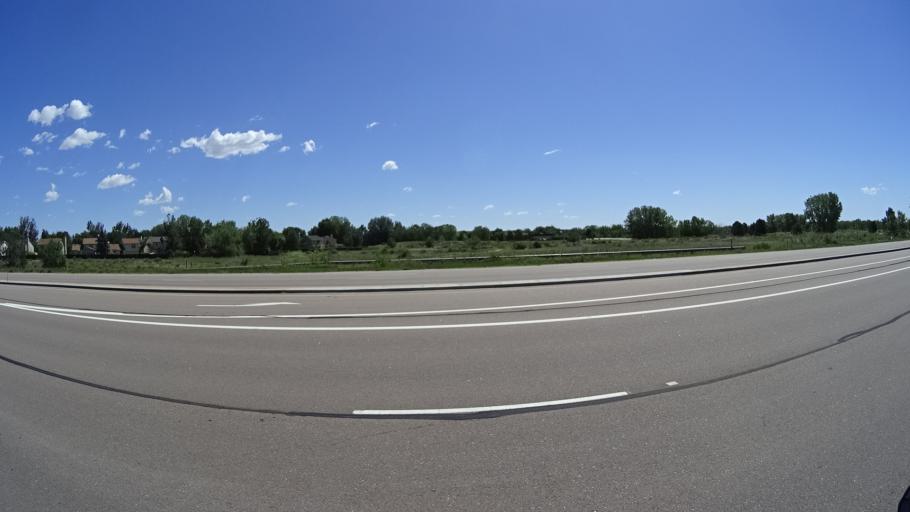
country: US
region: Colorado
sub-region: El Paso County
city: Security-Widefield
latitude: 38.7637
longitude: -104.6597
